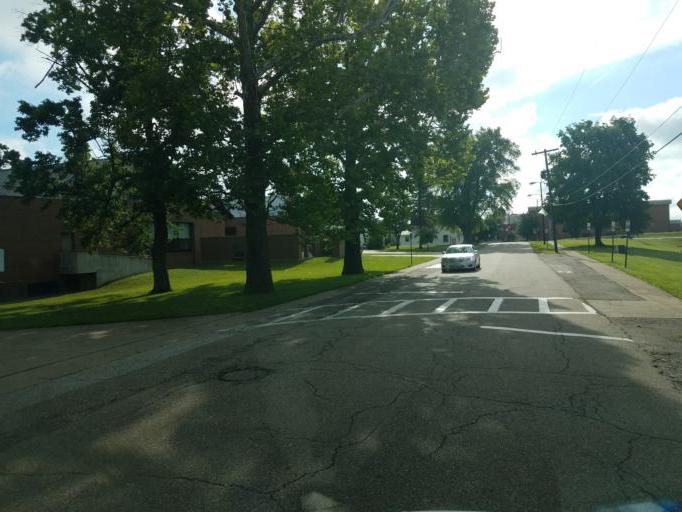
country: US
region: Ohio
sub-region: Gallia County
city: Gallipolis
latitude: 38.8795
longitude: -82.3797
